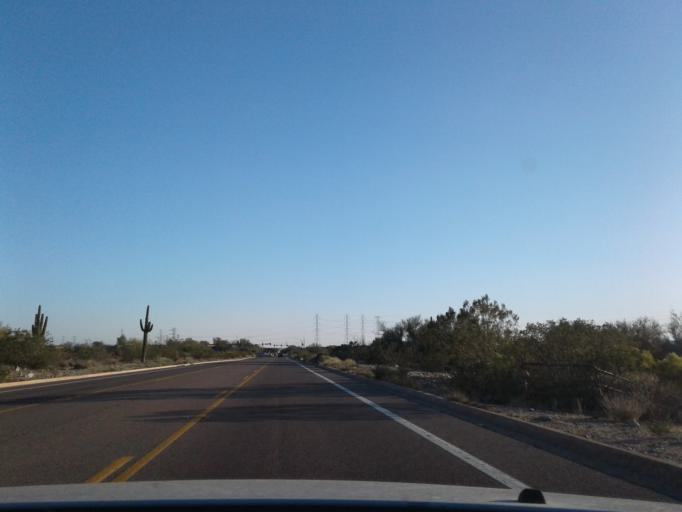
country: US
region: Arizona
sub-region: Maricopa County
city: Paradise Valley
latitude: 33.6440
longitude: -111.8785
